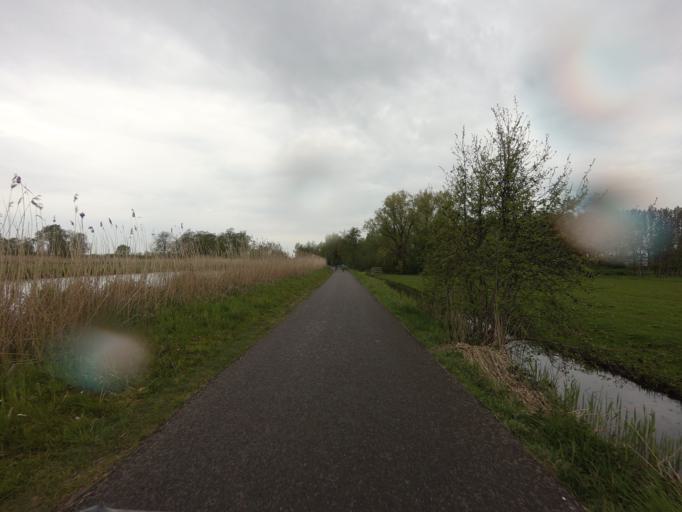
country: NL
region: South Holland
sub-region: Gemeente Gouda
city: Bloemendaal
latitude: 52.0201
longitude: 4.6728
